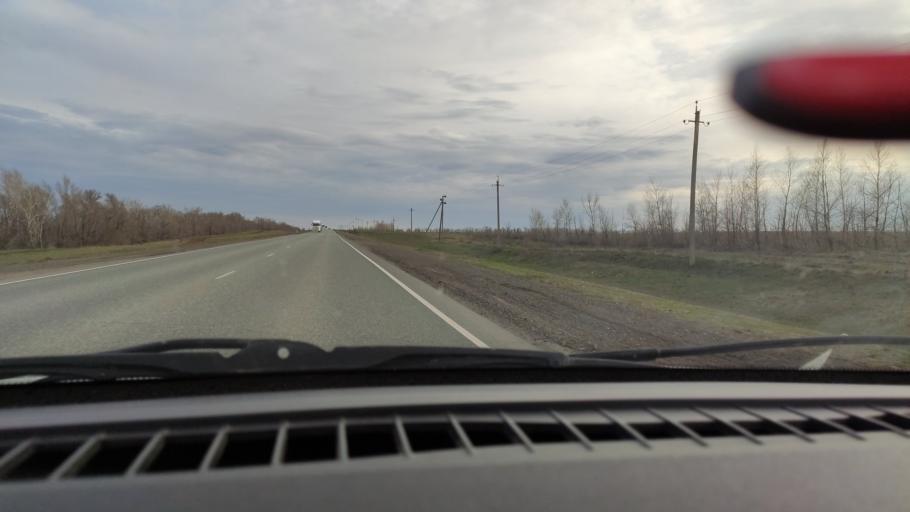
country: RU
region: Orenburg
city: Tatarskaya Kargala
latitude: 52.0080
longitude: 55.2020
